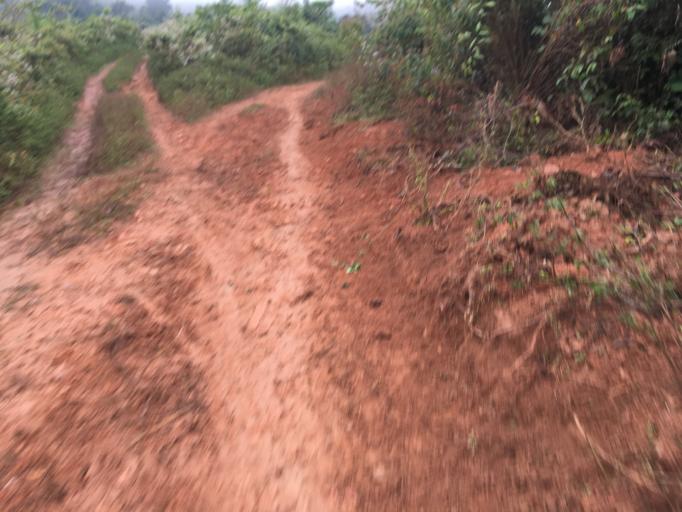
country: LA
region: Houaphan
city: Xamtay
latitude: 19.8957
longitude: 104.4629
